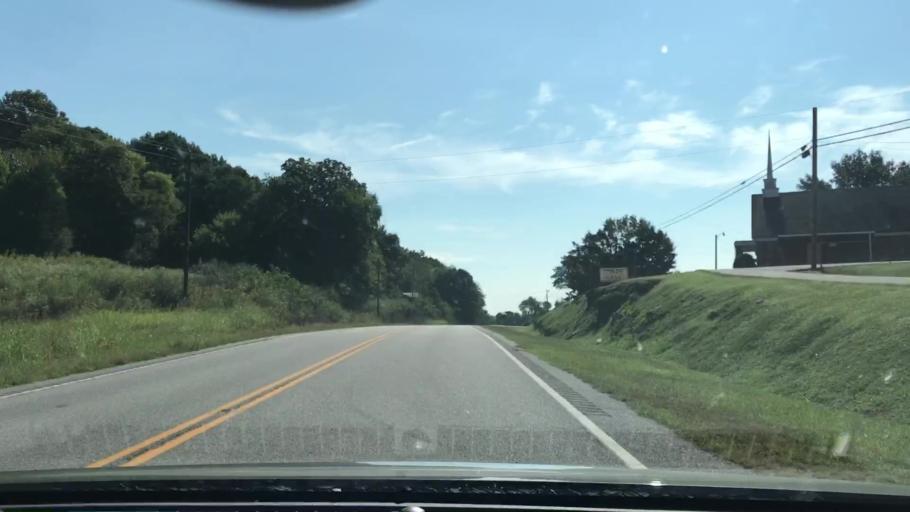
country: US
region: Tennessee
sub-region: Jackson County
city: Gainesboro
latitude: 36.3573
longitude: -85.7315
